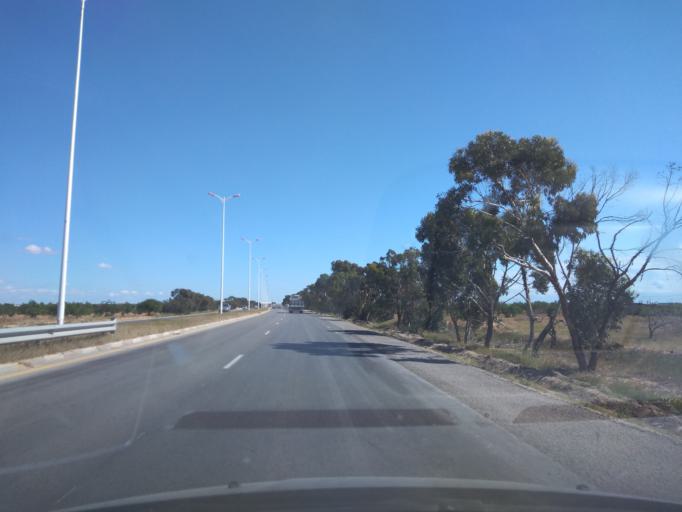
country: TN
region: Safaqis
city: Sfax
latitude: 34.8234
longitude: 10.7132
